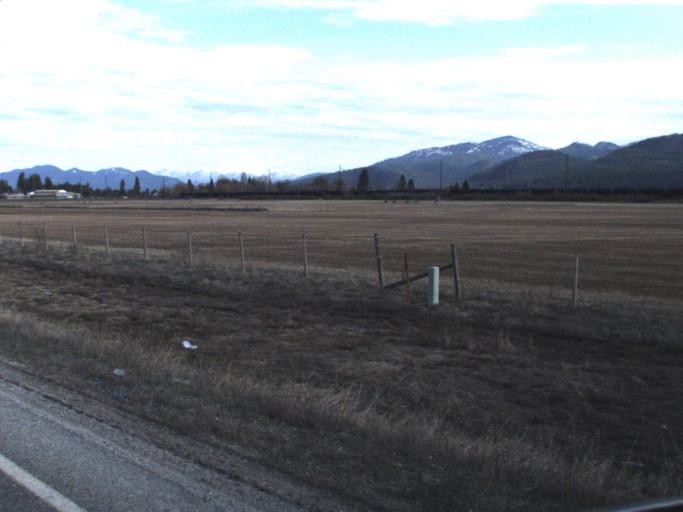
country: US
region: Washington
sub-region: Pend Oreille County
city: Newport
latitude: 48.3251
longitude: -117.2972
